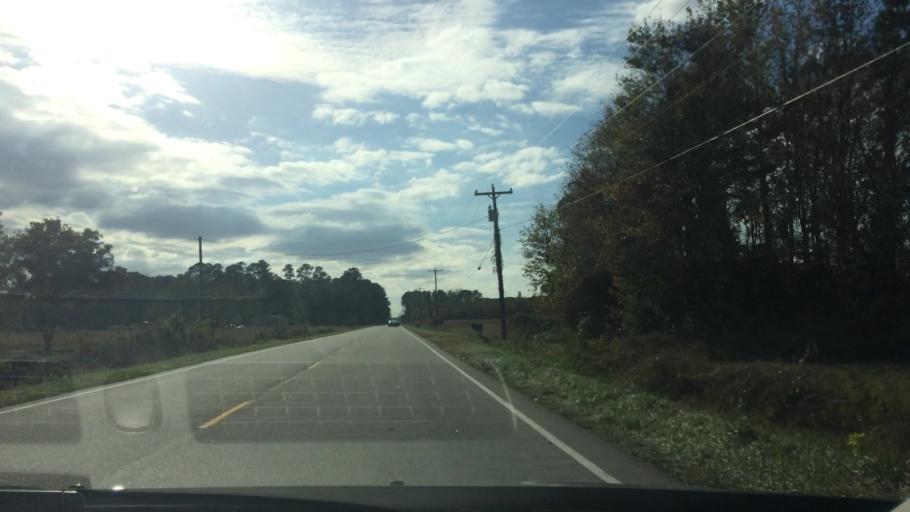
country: US
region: North Carolina
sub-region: Wayne County
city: Elroy
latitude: 35.4371
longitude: -77.8606
